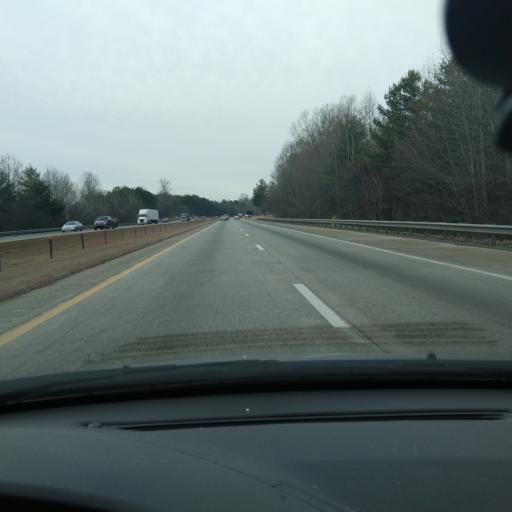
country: US
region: North Carolina
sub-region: Davidson County
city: Wallburg
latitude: 36.0676
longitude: -80.1658
